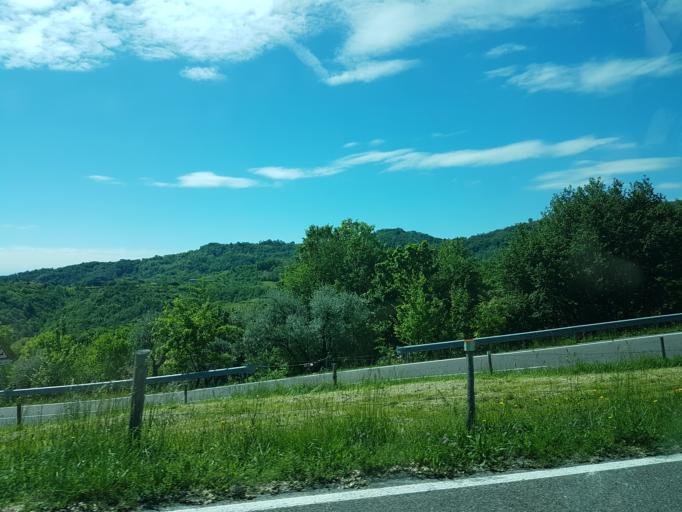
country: IT
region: Veneto
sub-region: Provincia di Vicenza
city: Pianezze
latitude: 45.7688
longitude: 11.6363
